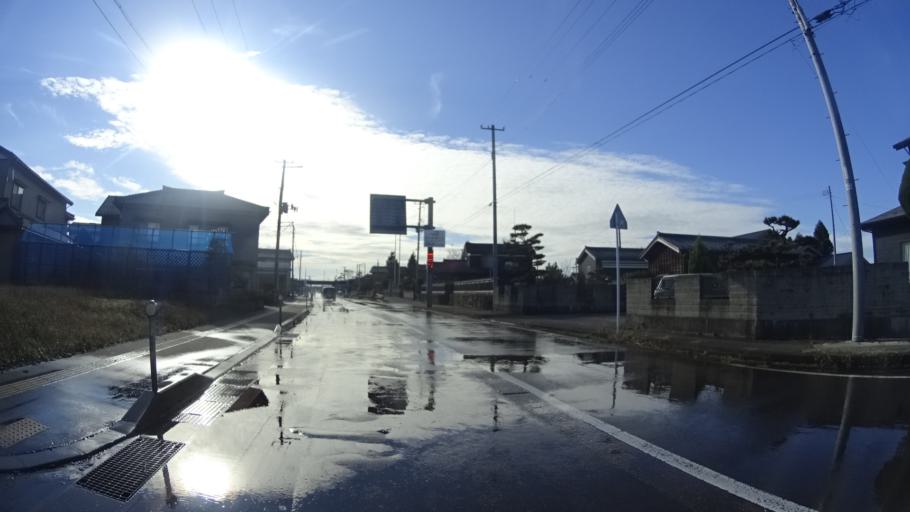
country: JP
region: Niigata
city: Yoshida-kasugacho
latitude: 37.6292
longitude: 138.8360
